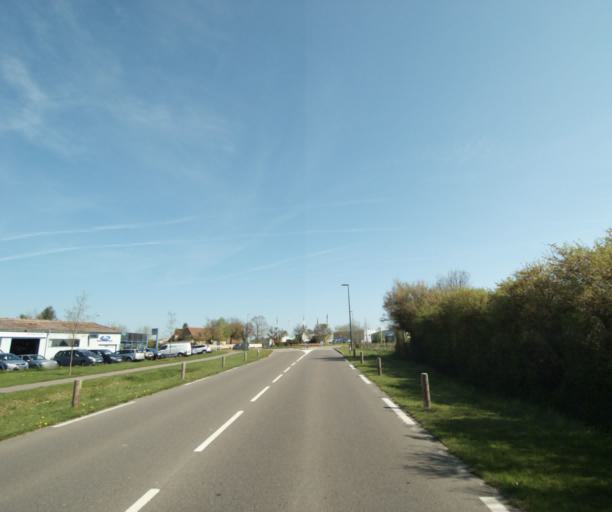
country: FR
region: Bourgogne
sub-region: Departement de Saone-et-Loire
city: Paray-le-Monial
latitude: 46.4650
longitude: 4.1174
